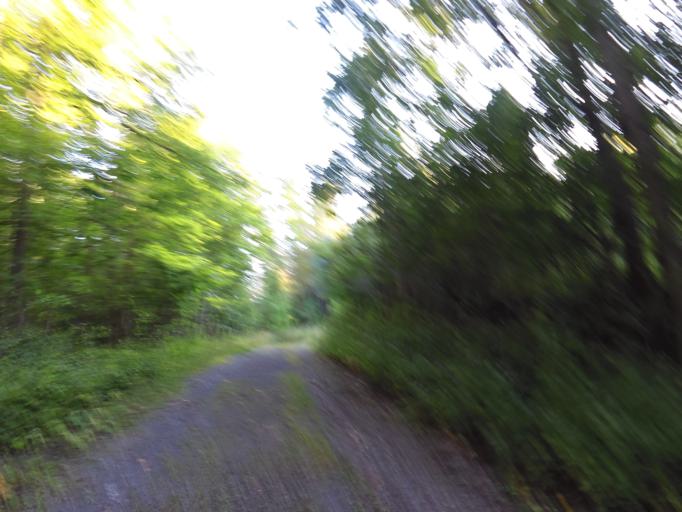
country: CA
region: Quebec
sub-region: Outaouais
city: Gatineau
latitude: 45.4591
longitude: -75.7257
